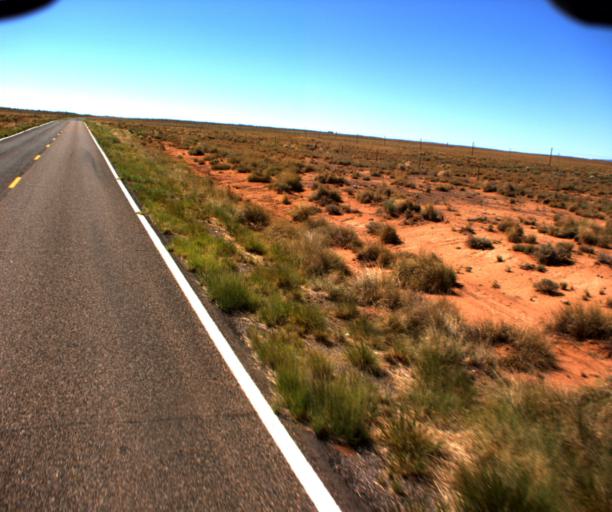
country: US
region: Arizona
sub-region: Coconino County
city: LeChee
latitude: 35.1324
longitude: -110.8820
